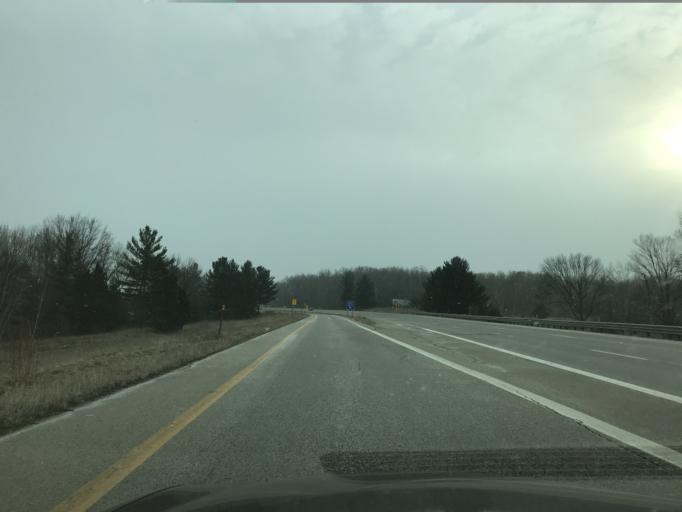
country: US
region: Michigan
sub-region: Clare County
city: Clare
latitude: 43.8541
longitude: -84.7789
